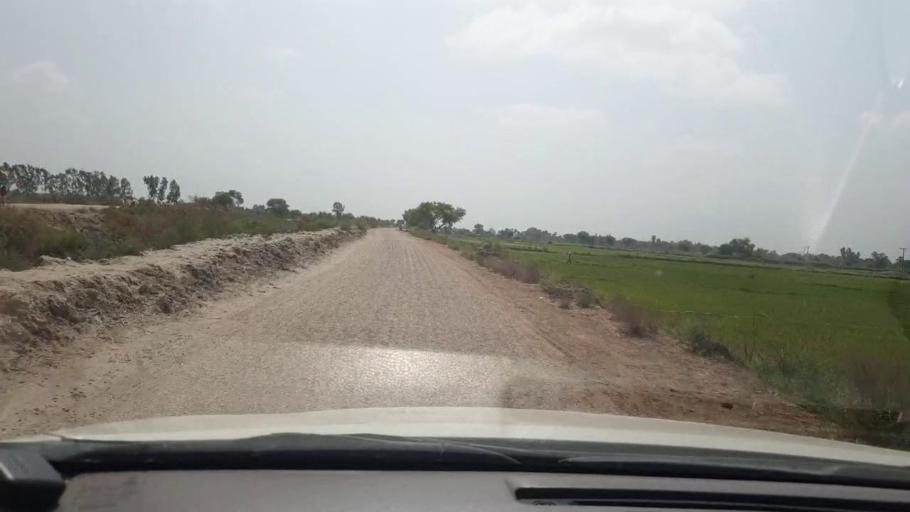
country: PK
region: Sindh
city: Shikarpur
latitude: 28.0099
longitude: 68.5659
